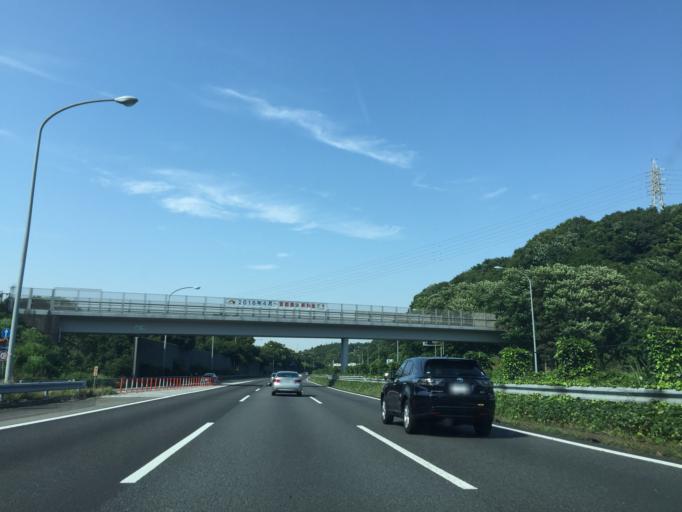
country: JP
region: Kanagawa
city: Minami-rinkan
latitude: 35.5090
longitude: 139.4848
